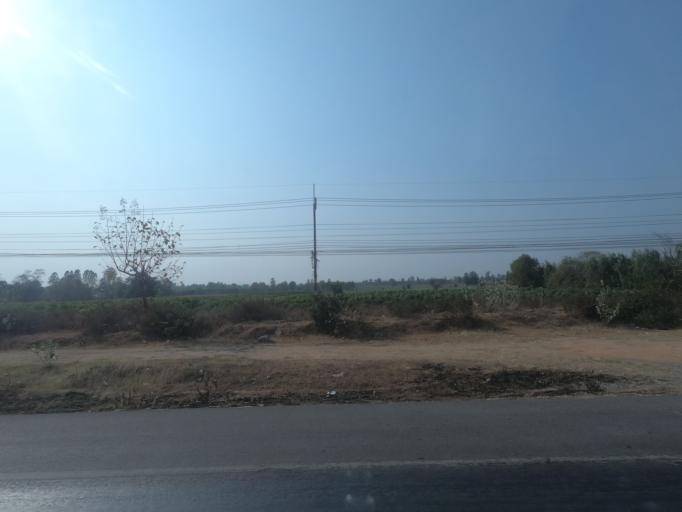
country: TH
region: Khon Kaen
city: Ban Haet
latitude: 16.2315
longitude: 102.7668
